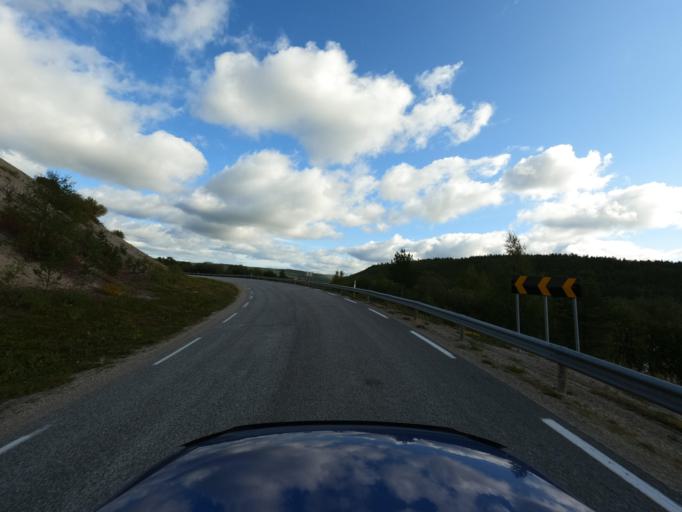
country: NO
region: Finnmark Fylke
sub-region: Karasjok
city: Karasjohka
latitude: 69.4373
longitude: 25.1706
